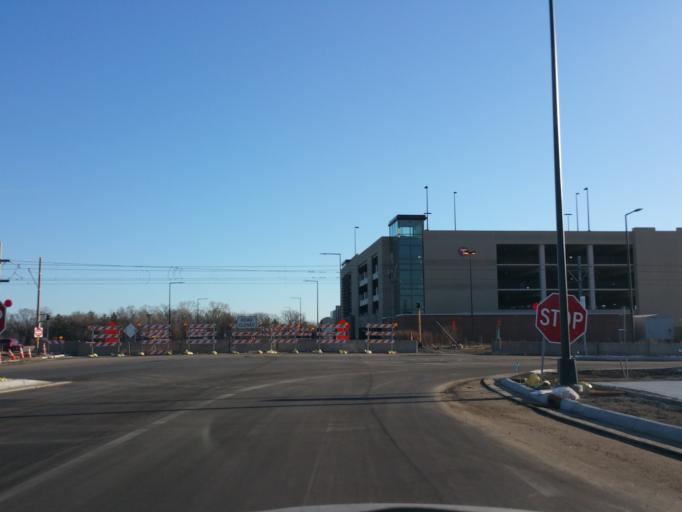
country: US
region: Minnesota
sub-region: Hennepin County
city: Richfield
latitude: 44.8569
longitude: -93.2299
